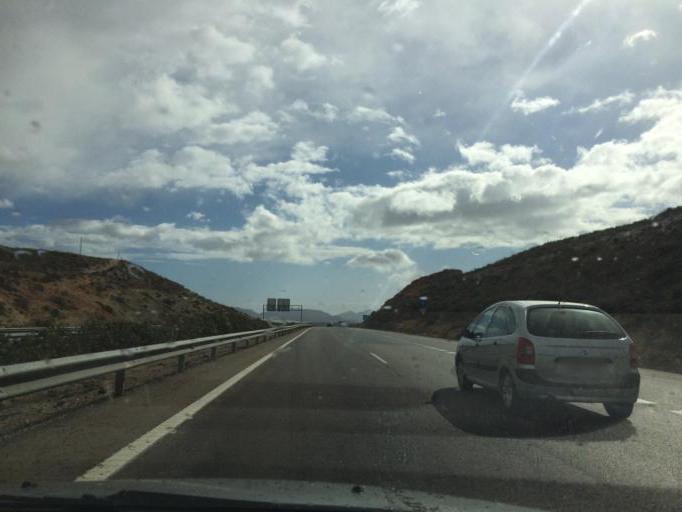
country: ES
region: Andalusia
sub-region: Provincia de Almeria
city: Retamar
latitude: 36.8636
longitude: -2.2652
